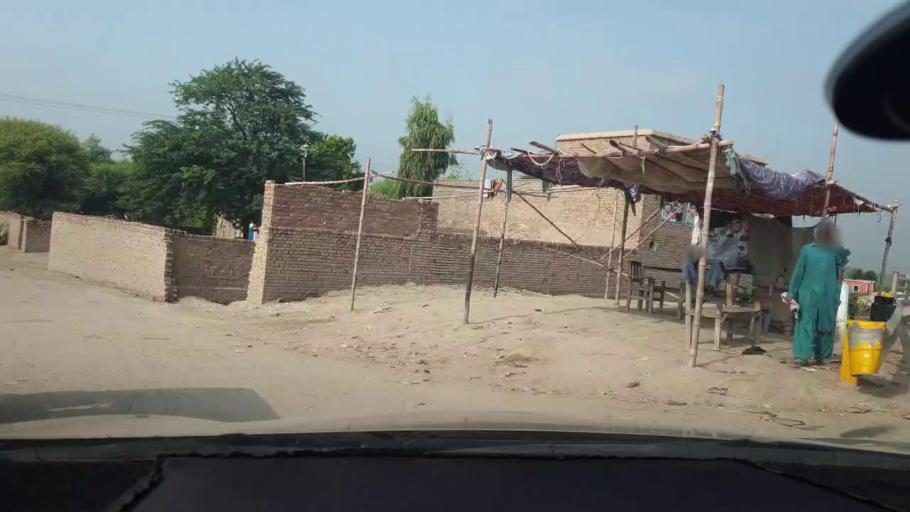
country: PK
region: Sindh
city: Kambar
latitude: 27.5048
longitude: 68.0138
